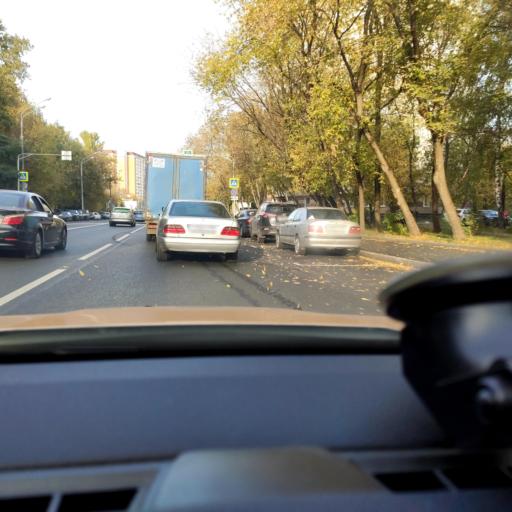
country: RU
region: Moscow
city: Leonovo
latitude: 55.8495
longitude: 37.6427
